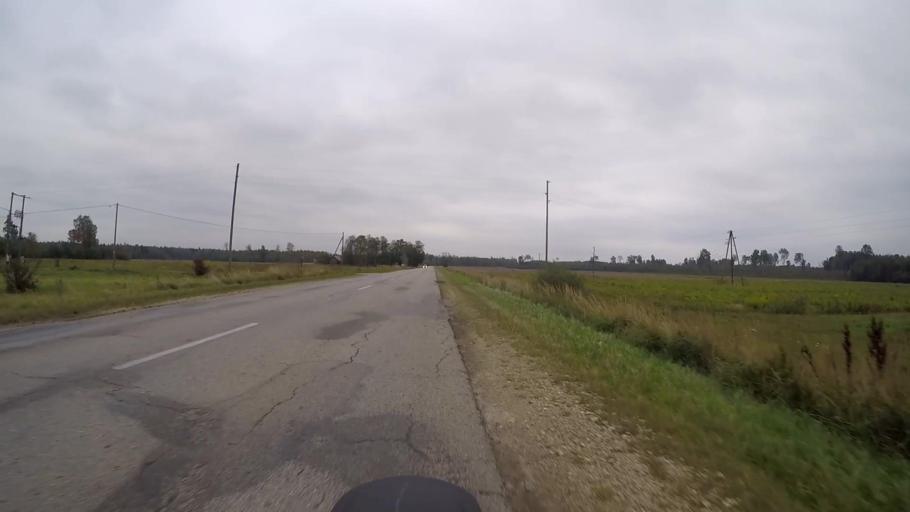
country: LV
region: Saulkrastu
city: Saulkrasti
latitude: 57.2751
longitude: 24.5359
